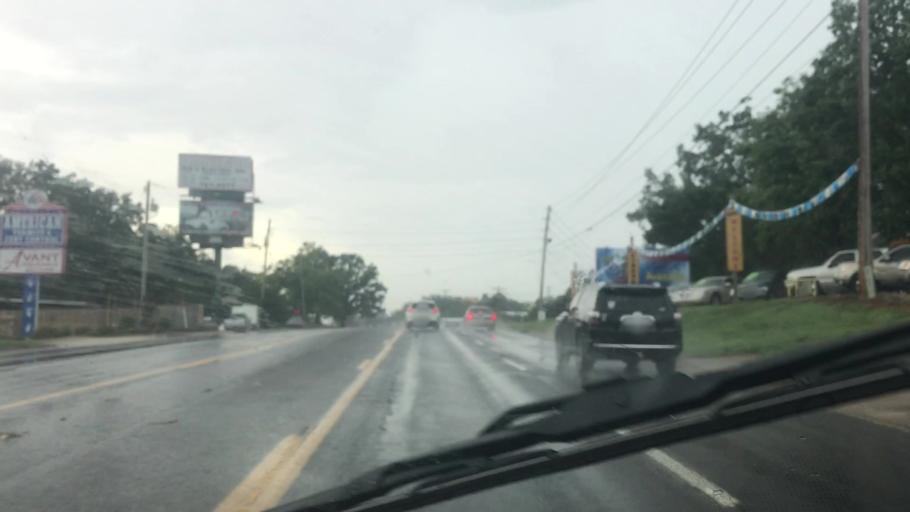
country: US
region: Arkansas
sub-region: Garland County
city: Rockwell
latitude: 34.4697
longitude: -93.1345
